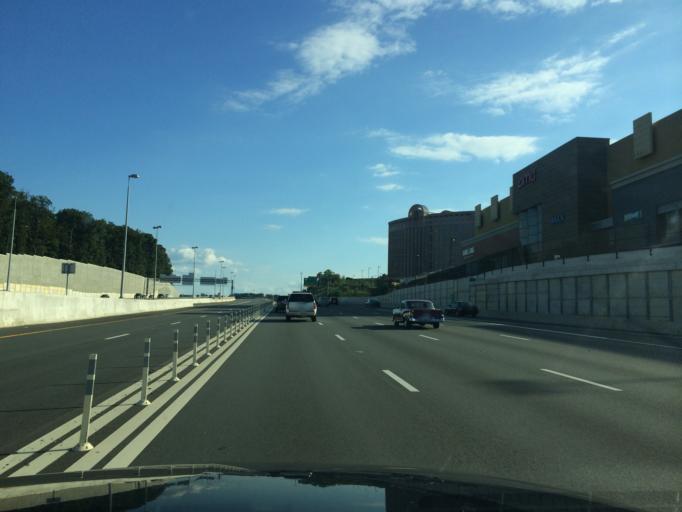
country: US
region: Virginia
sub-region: Fairfax County
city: Tysons Corner
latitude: 38.9190
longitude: -77.2173
